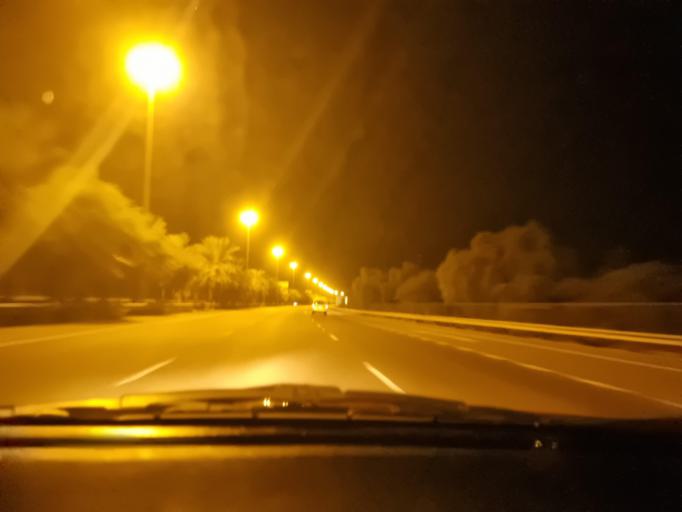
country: AE
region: Abu Dhabi
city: Al Ain
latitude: 24.1700
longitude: 55.2813
